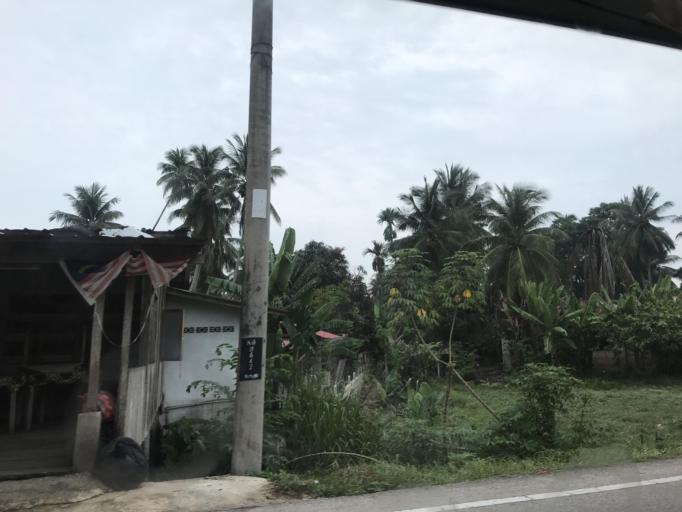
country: MY
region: Kelantan
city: Kota Bharu
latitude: 6.1720
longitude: 102.2295
